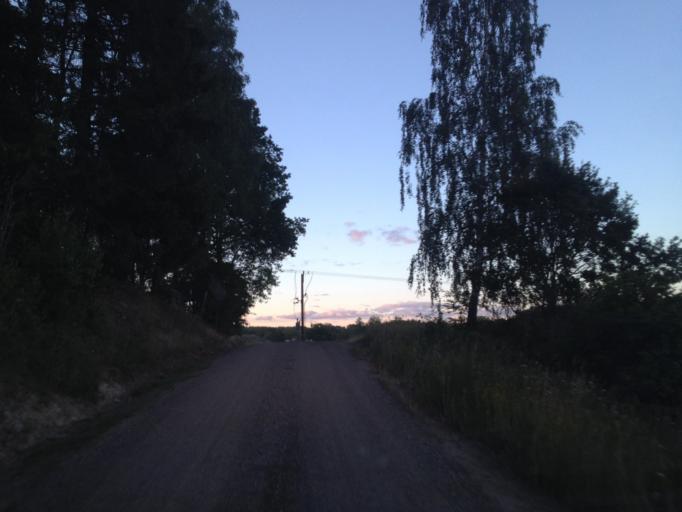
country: SE
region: Kalmar
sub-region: Vasterviks Kommun
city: Overum
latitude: 57.9895
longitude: 16.1756
